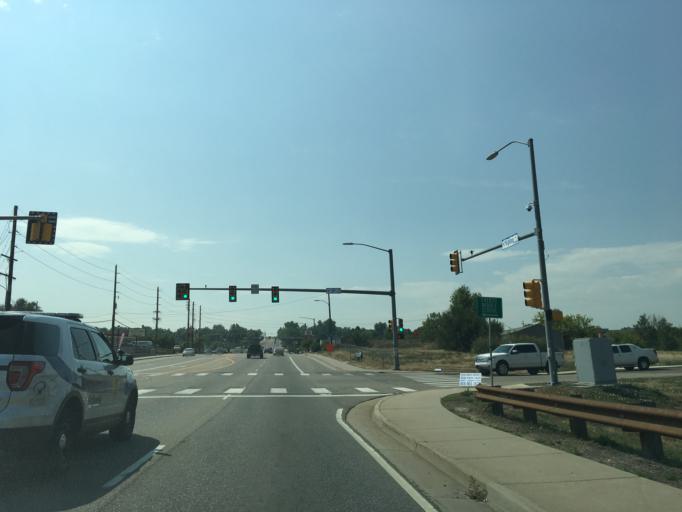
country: US
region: Colorado
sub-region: Jefferson County
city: Wheat Ridge
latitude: 39.7716
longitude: -105.1098
